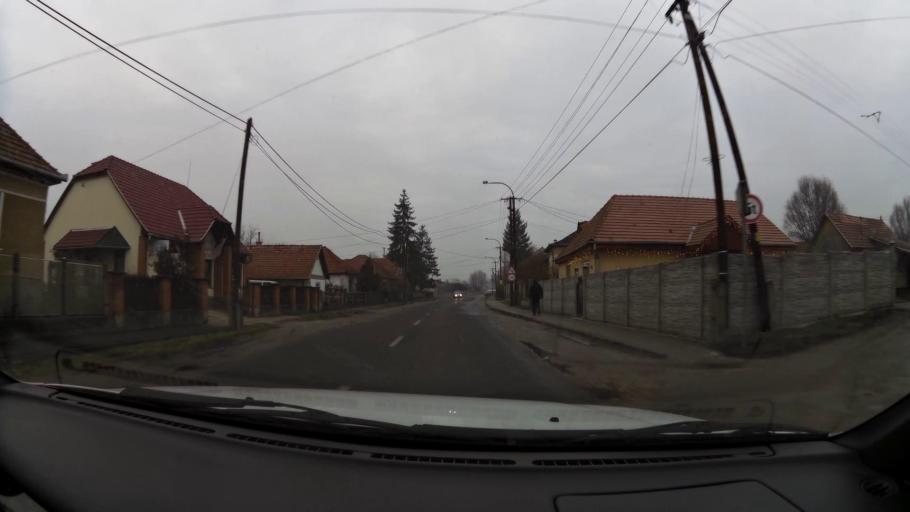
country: HU
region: Borsod-Abauj-Zemplen
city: Izsofalva
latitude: 48.3080
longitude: 20.6542
